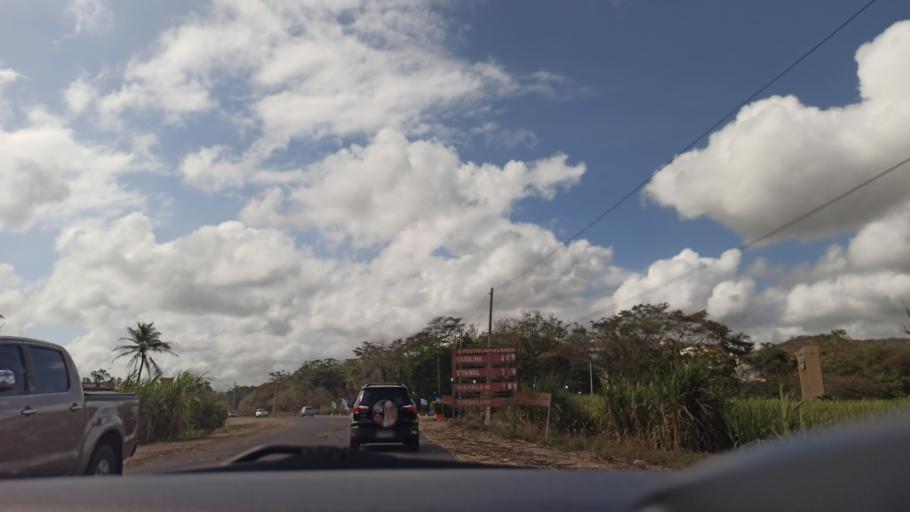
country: BR
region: Paraiba
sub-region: Juripiranga
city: Juripiranga
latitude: -7.4148
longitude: -35.2615
